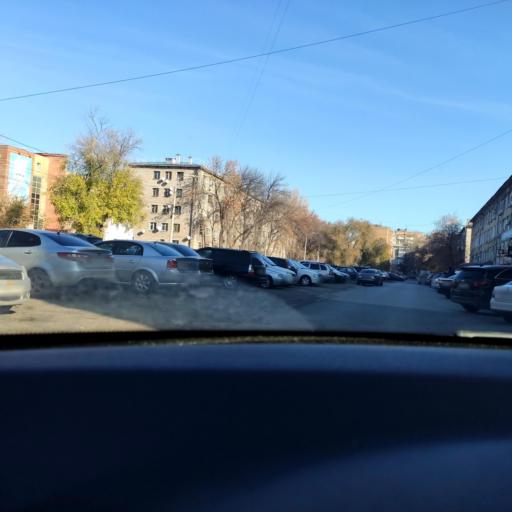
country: RU
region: Samara
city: Samara
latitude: 53.1939
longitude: 50.1315
